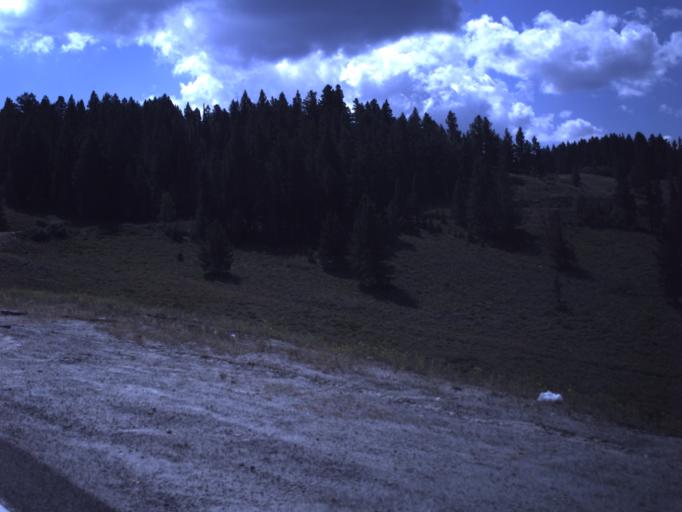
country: US
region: Idaho
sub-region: Bear Lake County
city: Paris
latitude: 41.9266
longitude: -111.4758
